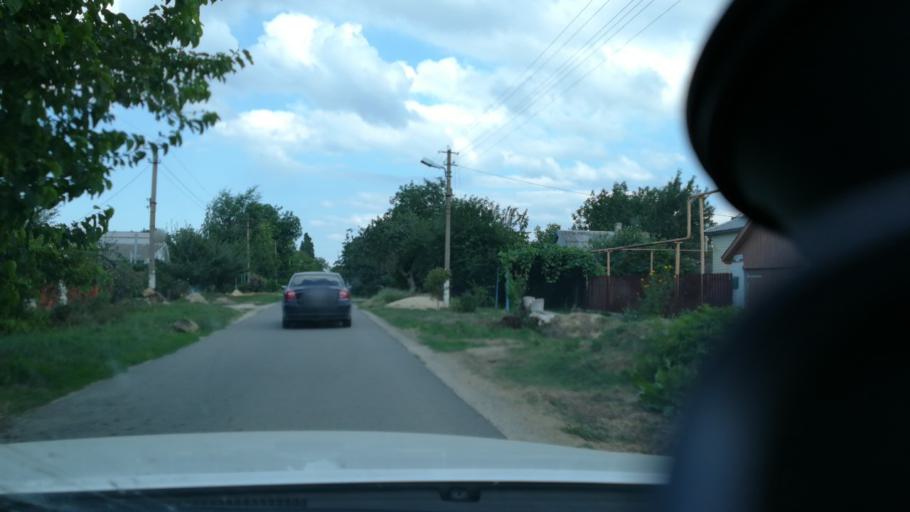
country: RU
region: Krasnodarskiy
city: Yurovka
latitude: 45.1172
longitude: 37.4161
